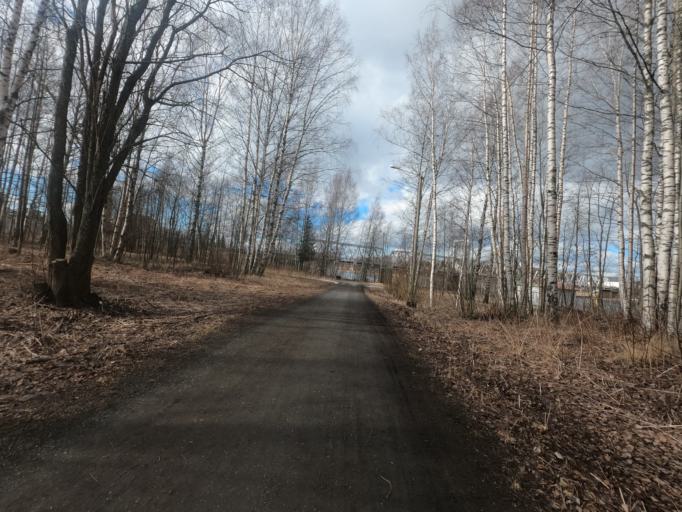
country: FI
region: North Karelia
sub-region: Joensuu
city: Joensuu
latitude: 62.6058
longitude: 29.7821
